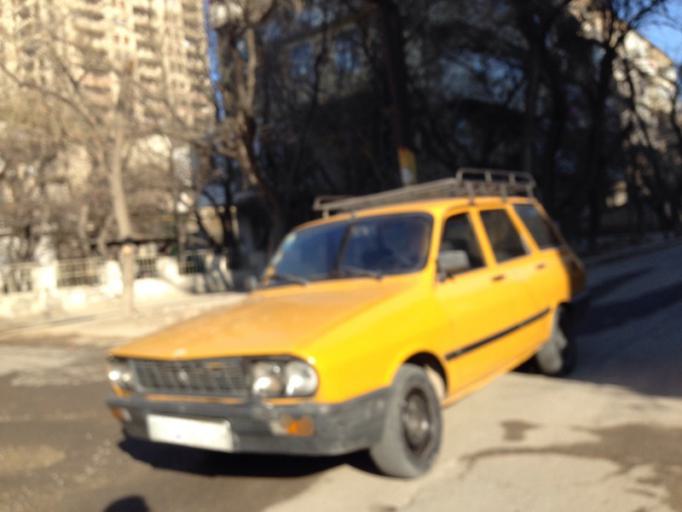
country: AZ
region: Baki
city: Baku
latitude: 40.4023
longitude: 49.8742
